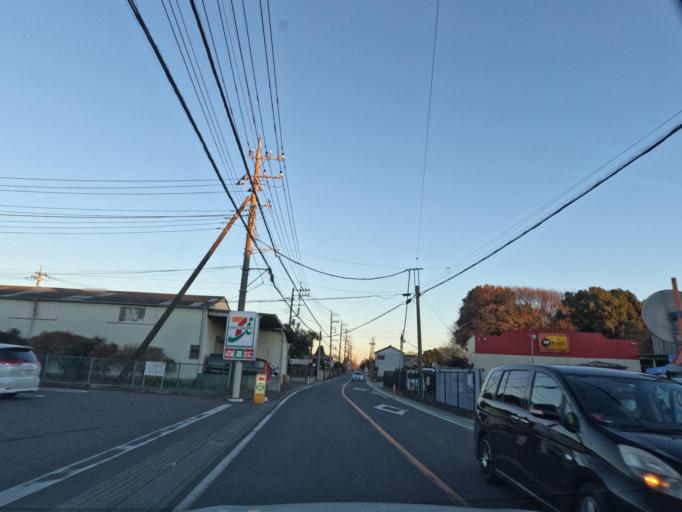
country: JP
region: Saitama
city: Iwatsuki
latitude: 35.9821
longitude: 139.7021
